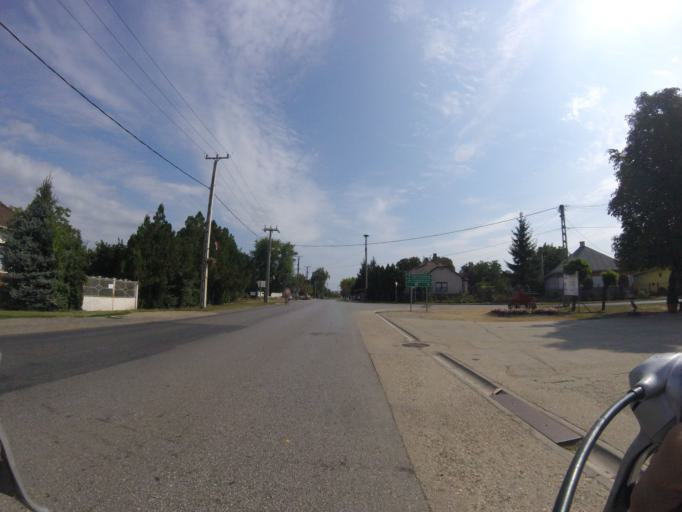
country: HU
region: Szabolcs-Szatmar-Bereg
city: Kemecse
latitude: 48.0671
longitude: 21.7987
